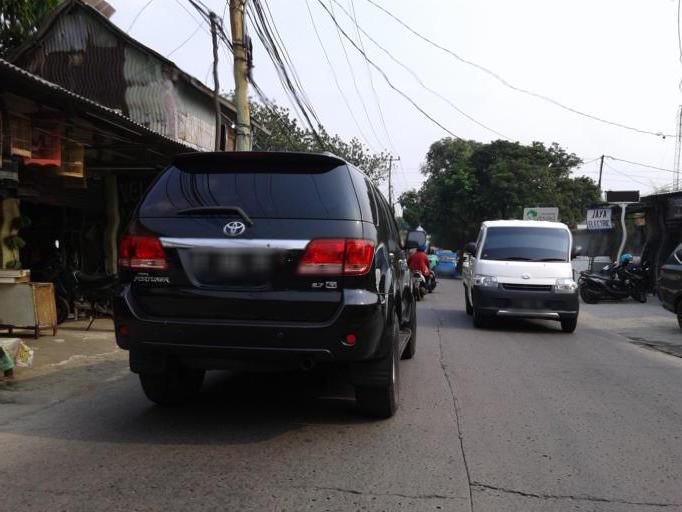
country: ID
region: West Java
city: Pamulang
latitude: -6.3563
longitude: 106.7755
